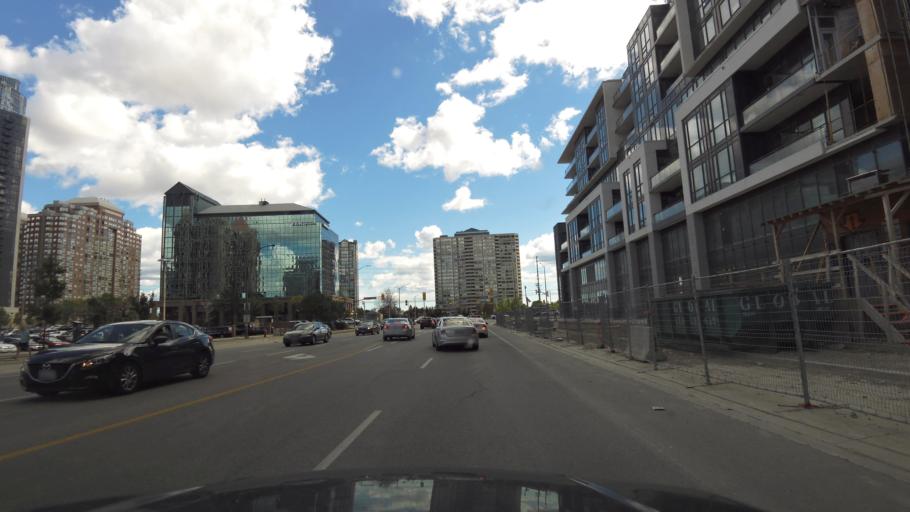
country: CA
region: Ontario
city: Mississauga
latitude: 43.5859
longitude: -79.6460
